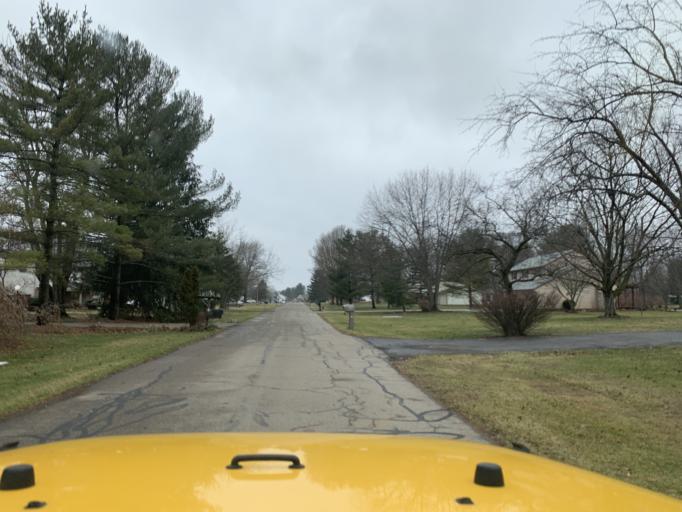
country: US
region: Ohio
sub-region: Franklin County
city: New Albany
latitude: 40.0933
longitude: -82.8053
